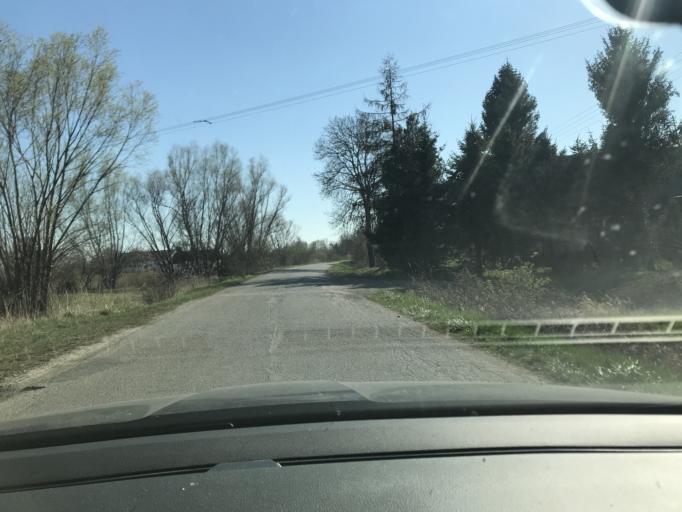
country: PL
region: Pomeranian Voivodeship
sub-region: Powiat nowodworski
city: Sztutowo
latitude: 54.3047
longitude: 19.1503
